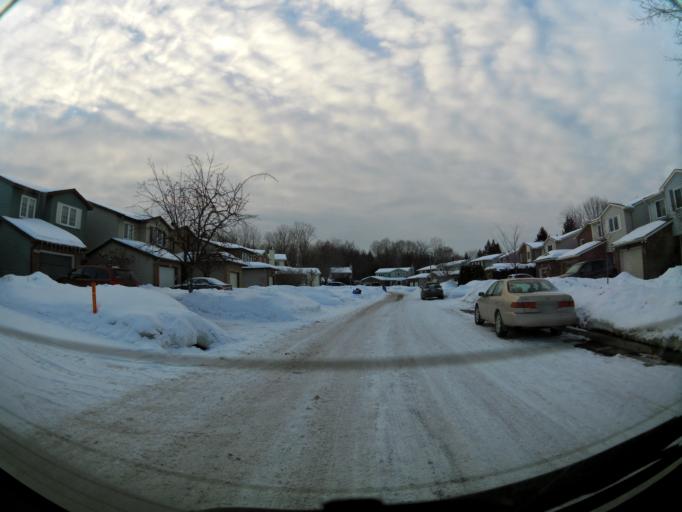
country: CA
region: Quebec
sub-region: Outaouais
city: Gatineau
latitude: 45.4579
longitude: -75.5437
